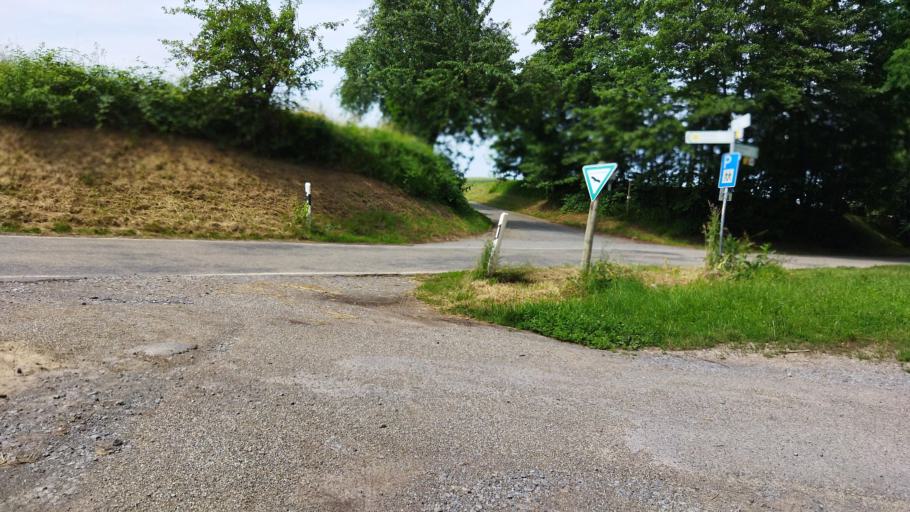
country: DE
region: Baden-Wuerttemberg
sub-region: Karlsruhe Region
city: Sulzfeld
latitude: 49.0803
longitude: 8.8901
